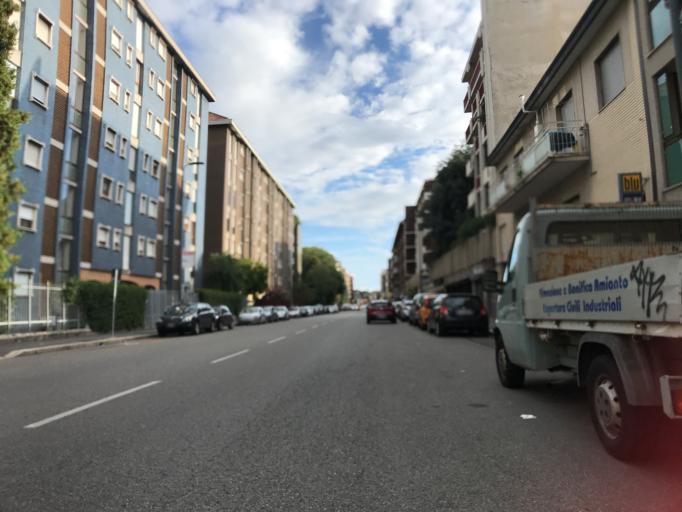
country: IT
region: Lombardy
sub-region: Citta metropolitana di Milano
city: Sesto San Giovanni
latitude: 45.4904
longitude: 9.2370
